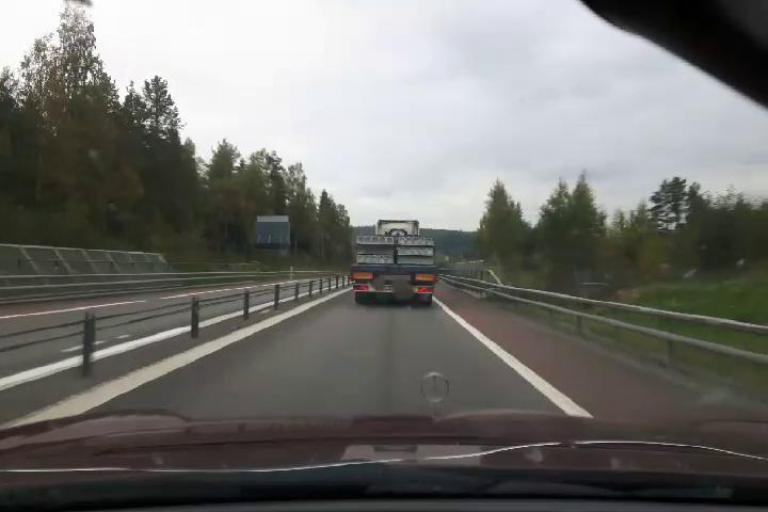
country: SE
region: Vaesternorrland
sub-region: Haernoesands Kommun
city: Haernoesand
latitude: 62.7736
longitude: 17.9178
